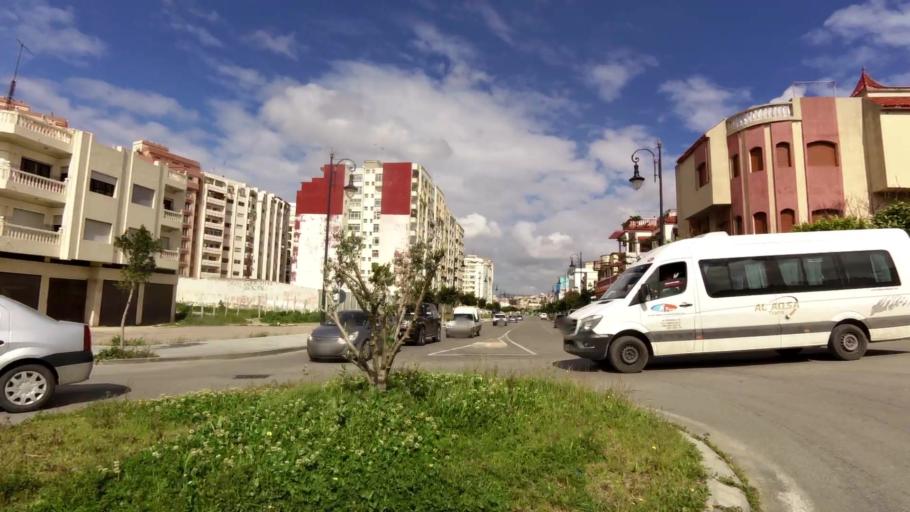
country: MA
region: Tanger-Tetouan
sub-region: Tanger-Assilah
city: Tangier
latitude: 35.7647
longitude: -5.8085
